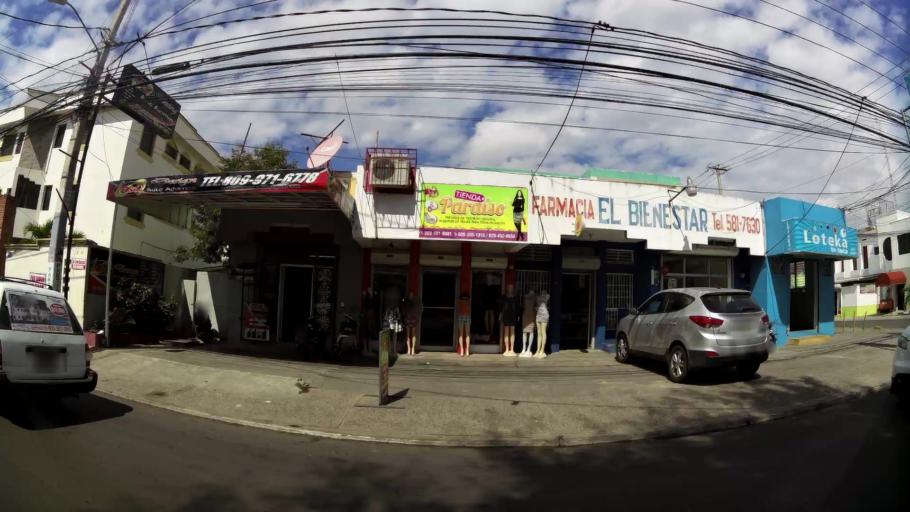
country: DO
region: Santiago
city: Santiago de los Caballeros
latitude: 19.4688
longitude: -70.6923
